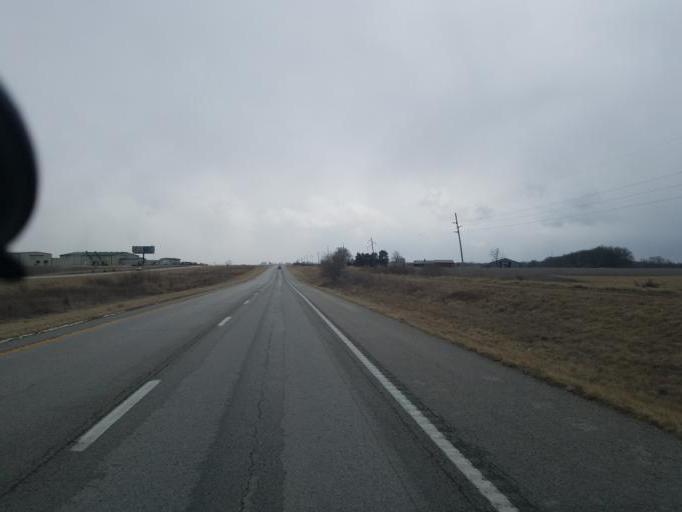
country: US
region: Missouri
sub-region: Randolph County
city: Moberly
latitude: 39.5454
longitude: -92.4521
